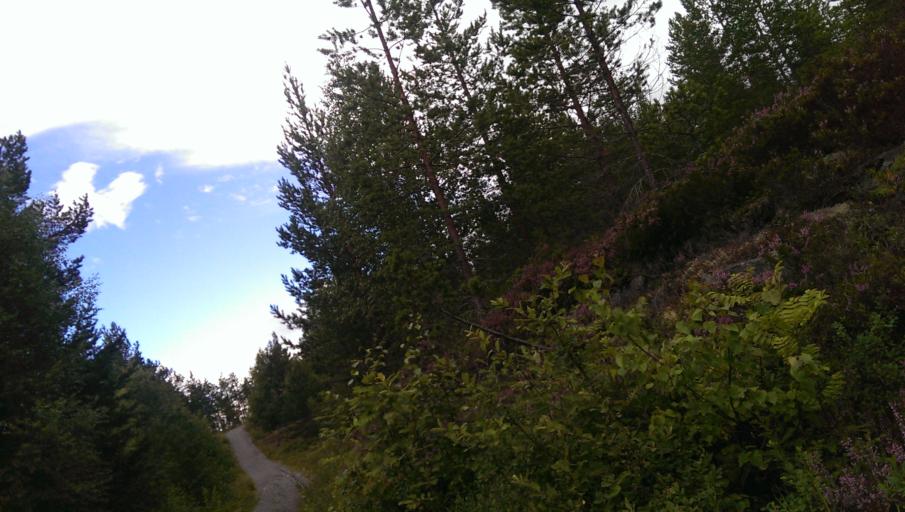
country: NO
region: Buskerud
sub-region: Kongsberg
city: Kongsberg
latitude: 59.6544
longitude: 9.6149
